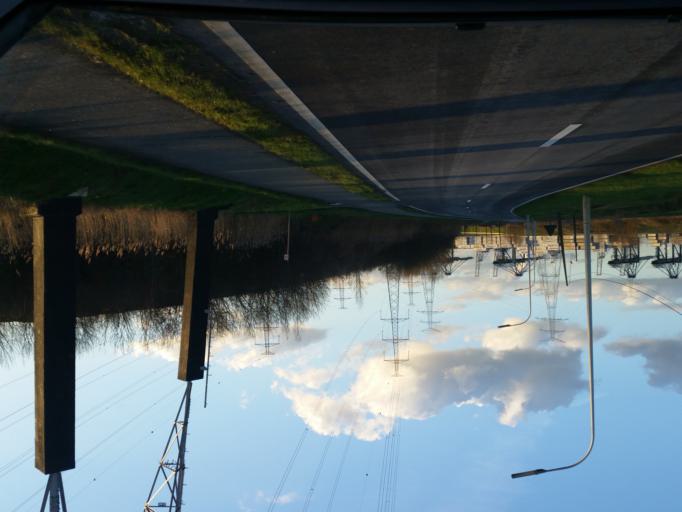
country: BE
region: Flanders
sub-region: Provincie Oost-Vlaanderen
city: Beveren
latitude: 51.3064
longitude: 4.2537
